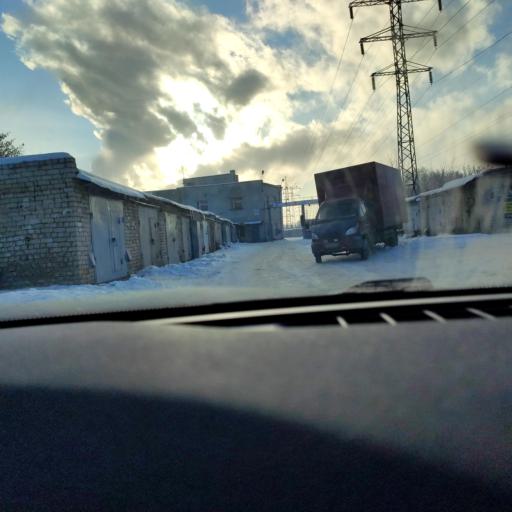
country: RU
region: Samara
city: Smyshlyayevka
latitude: 53.2077
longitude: 50.2872
